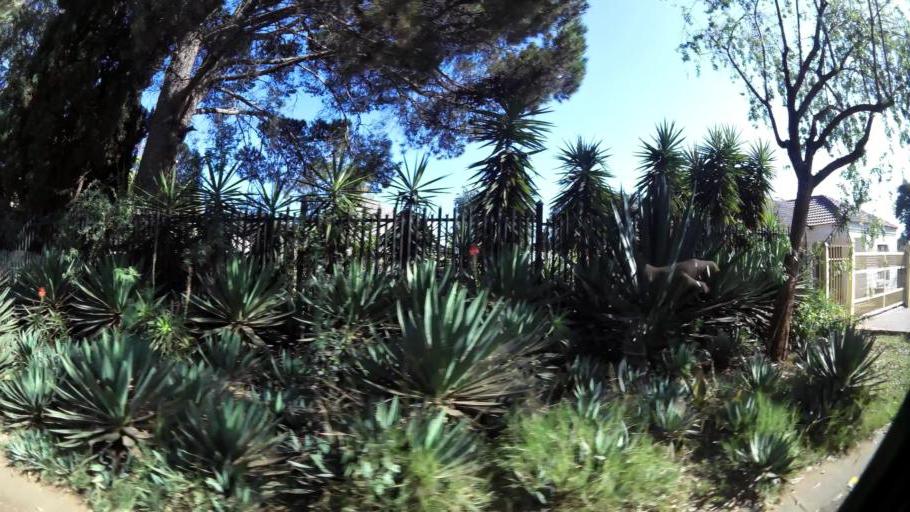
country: ZA
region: North-West
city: Ga-Rankuwa
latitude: -25.6689
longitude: 28.0919
